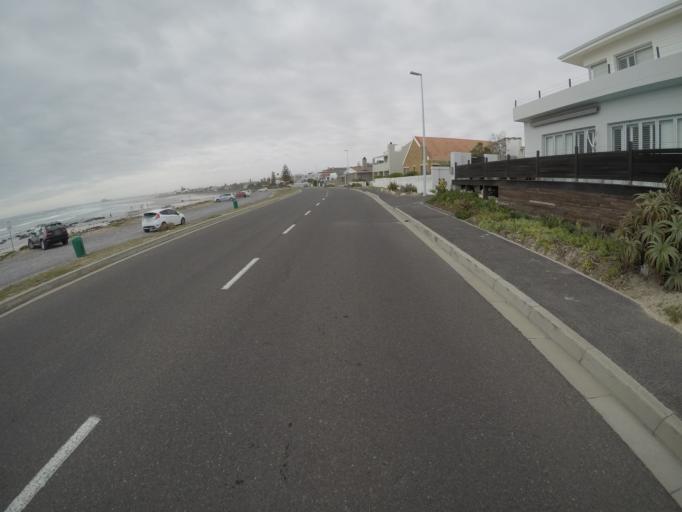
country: ZA
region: Western Cape
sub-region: City of Cape Town
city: Sunset Beach
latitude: -33.7215
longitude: 18.4438
